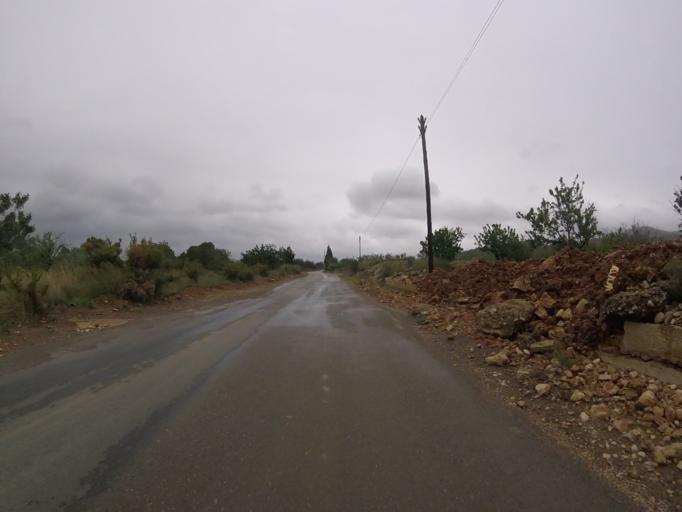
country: ES
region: Valencia
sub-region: Provincia de Castello
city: Alcoceber
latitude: 40.2423
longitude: 0.2490
